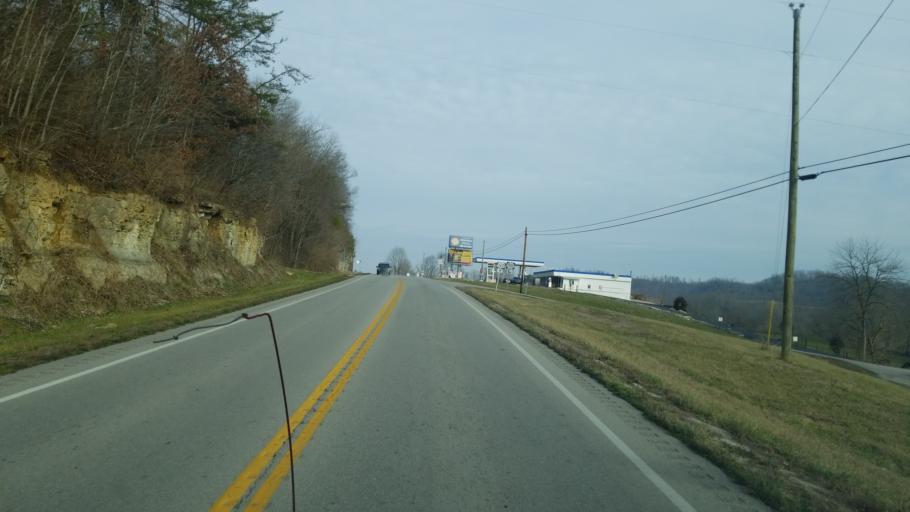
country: US
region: Kentucky
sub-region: Casey County
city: Liberty
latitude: 37.3599
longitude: -84.8674
